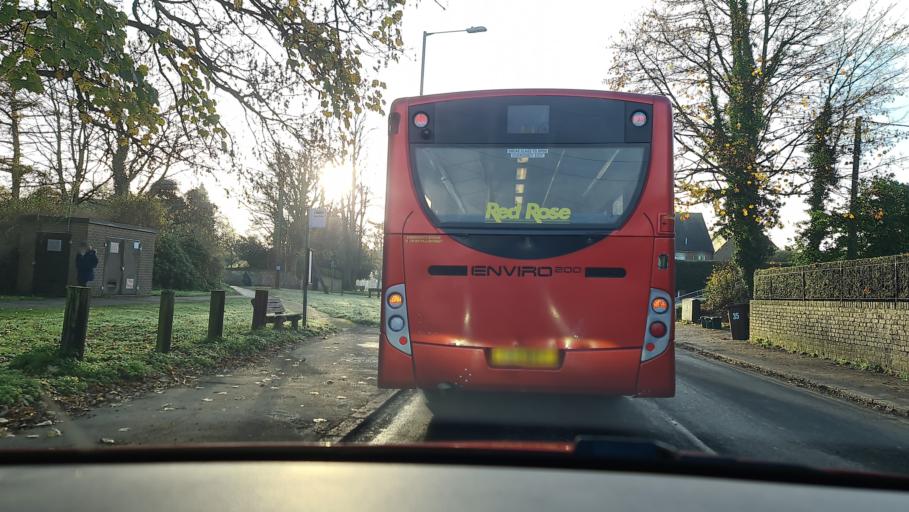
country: GB
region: England
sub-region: Buckinghamshire
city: Wendover
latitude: 51.7654
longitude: -0.7438
